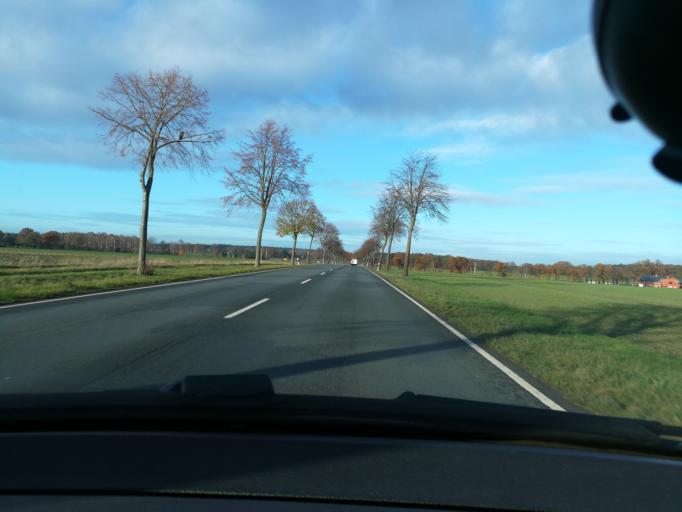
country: DE
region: Lower Saxony
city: Uchte
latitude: 52.5115
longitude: 8.9025
